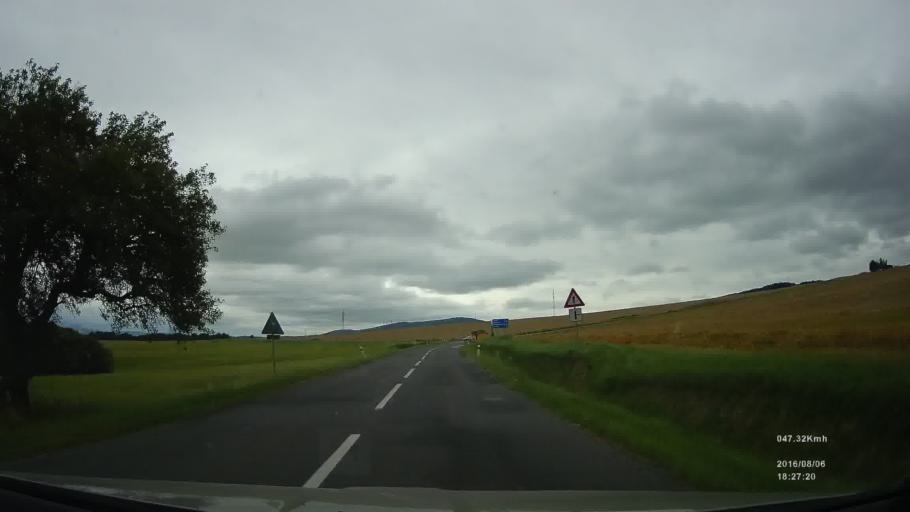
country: SK
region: Presovsky
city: Svidnik
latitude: 49.2818
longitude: 21.5698
